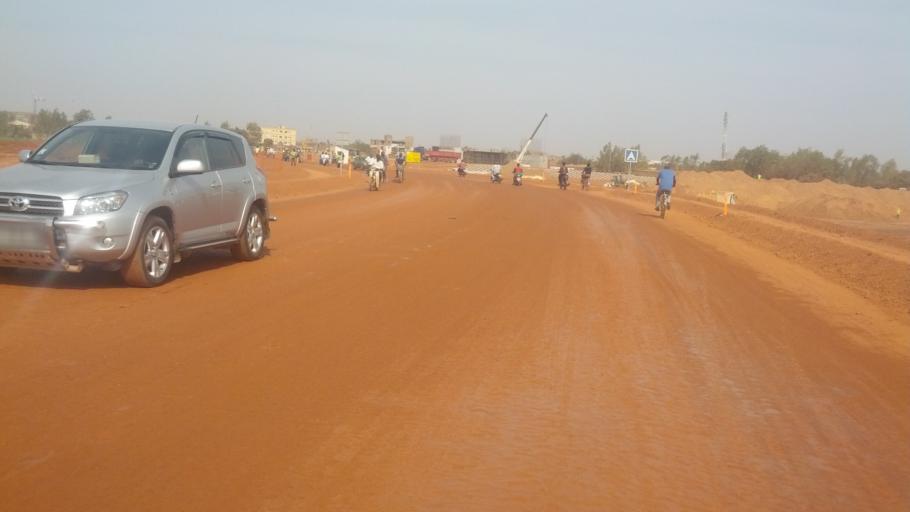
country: BF
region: Centre
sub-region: Kadiogo Province
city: Ouagadougou
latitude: 12.3833
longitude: -1.5564
